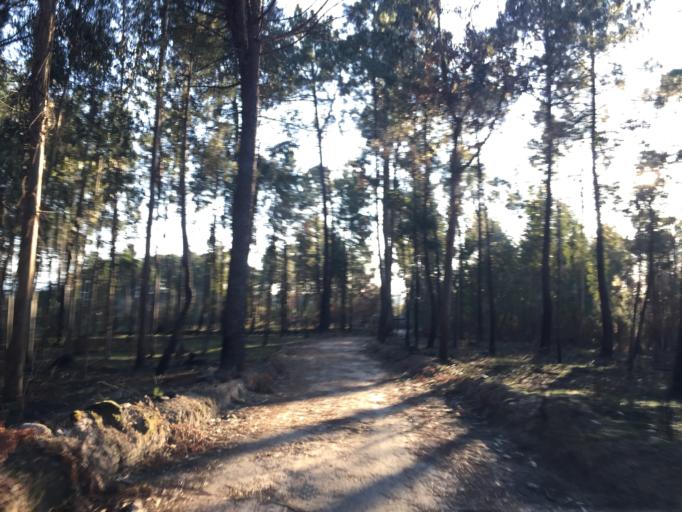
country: PT
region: Viseu
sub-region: Concelho de Carregal do Sal
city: Carregal do Sal
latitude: 40.4621
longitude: -7.9197
